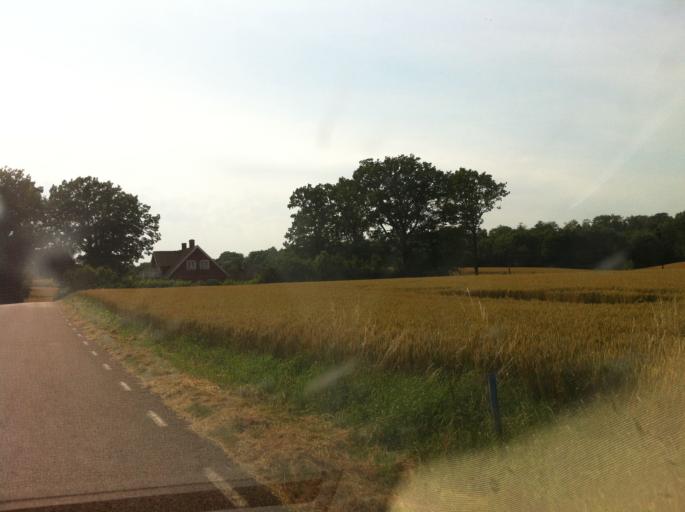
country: SE
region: Skane
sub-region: Eslovs Kommun
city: Stehag
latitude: 55.9592
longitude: 13.3155
